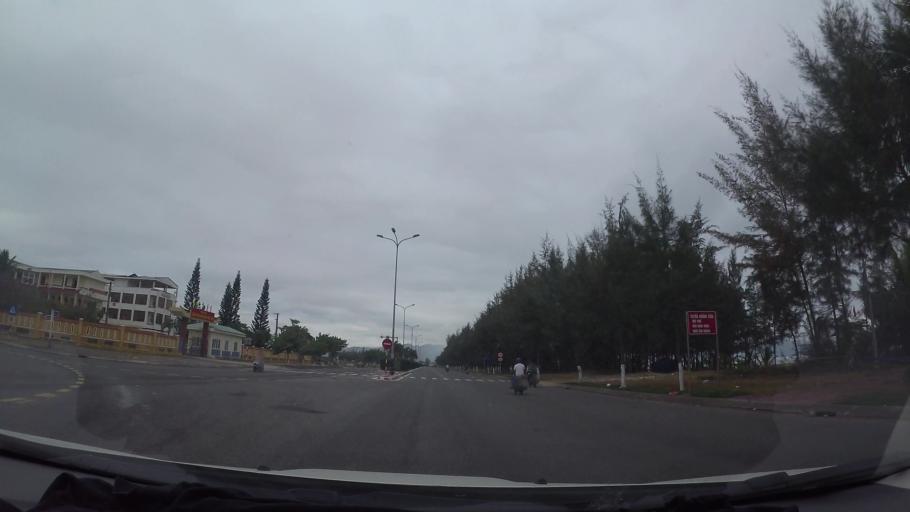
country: VN
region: Da Nang
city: Lien Chieu
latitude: 16.0921
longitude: 108.1497
